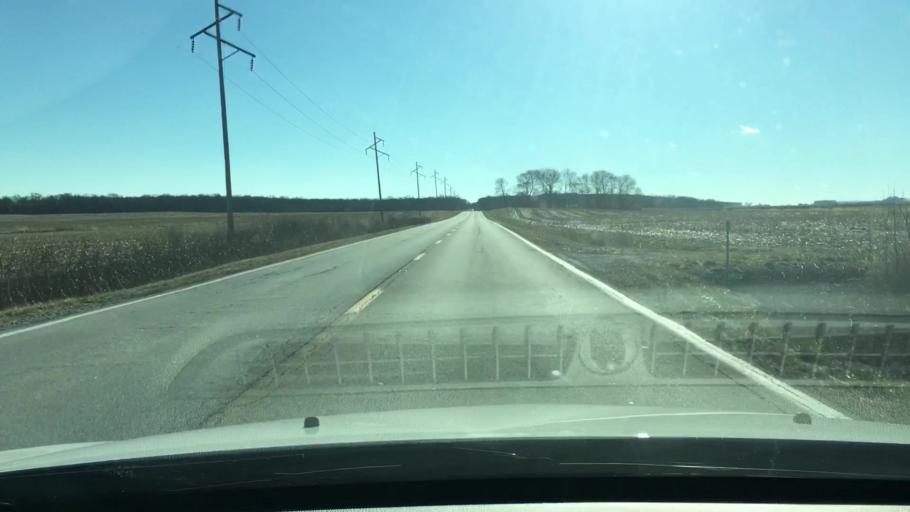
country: US
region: Illinois
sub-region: Morgan County
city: Meredosia
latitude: 39.9203
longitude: -90.4945
